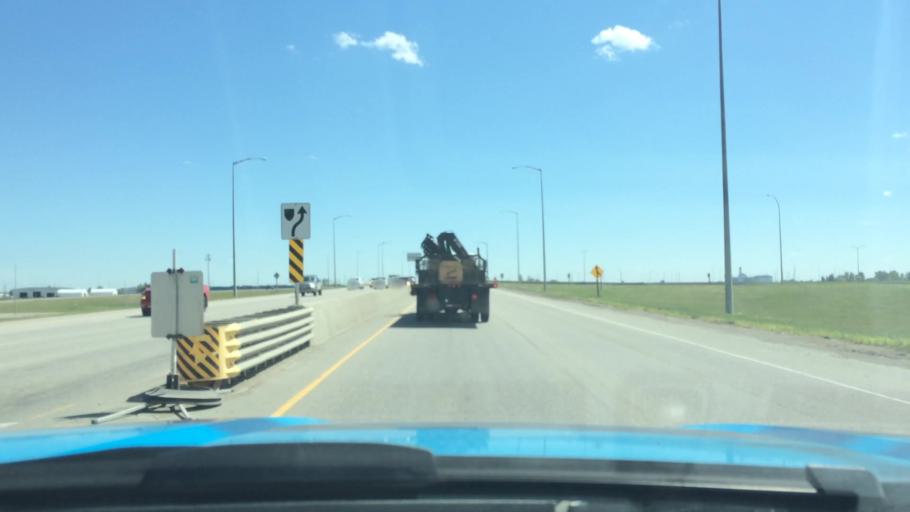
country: CA
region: Alberta
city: Chestermere
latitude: 50.9795
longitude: -113.9246
